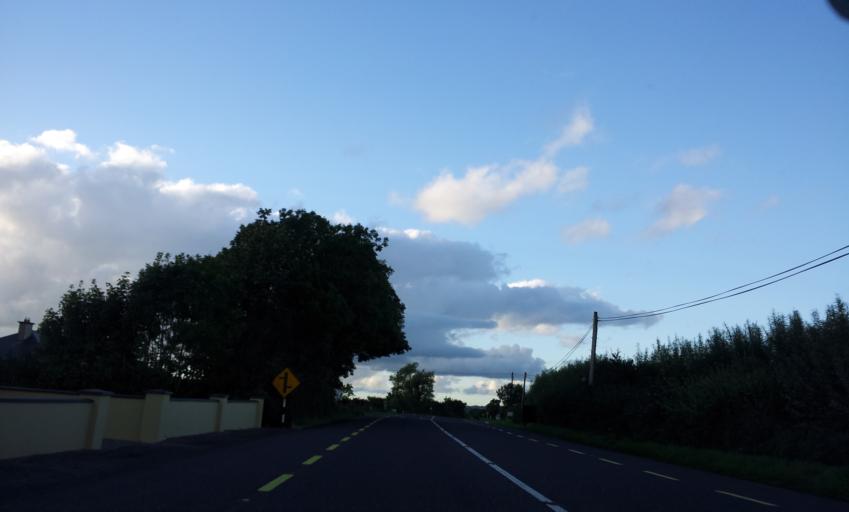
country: IE
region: Munster
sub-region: County Limerick
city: Abbeyfeale
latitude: 52.3604
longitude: -9.3248
